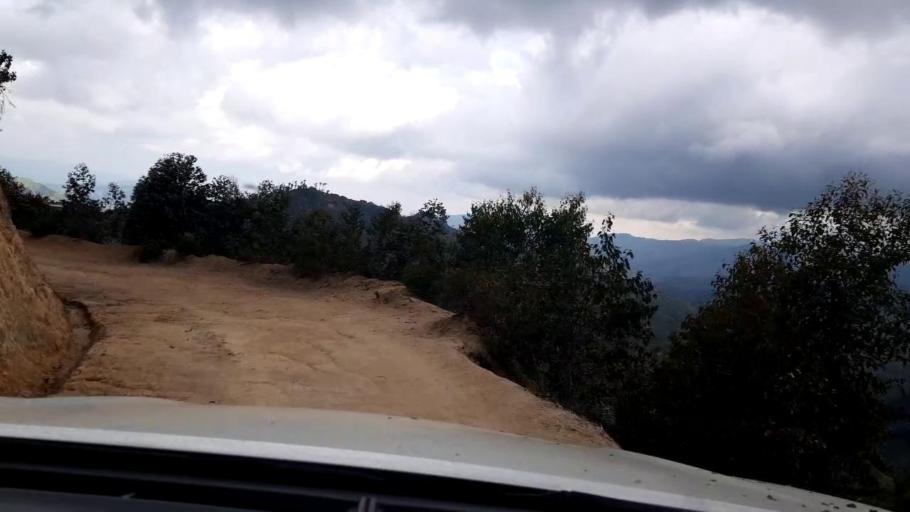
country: RW
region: Western Province
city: Kibuye
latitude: -1.8957
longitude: 29.5274
